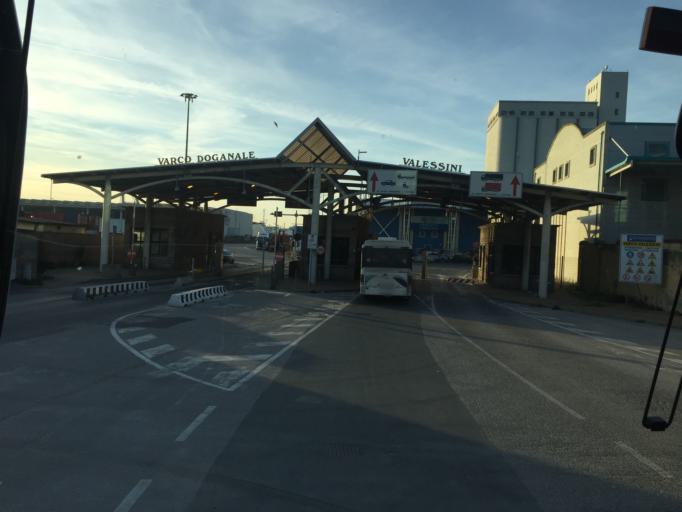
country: IT
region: Tuscany
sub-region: Provincia di Livorno
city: Livorno
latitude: 43.5612
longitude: 10.3071
